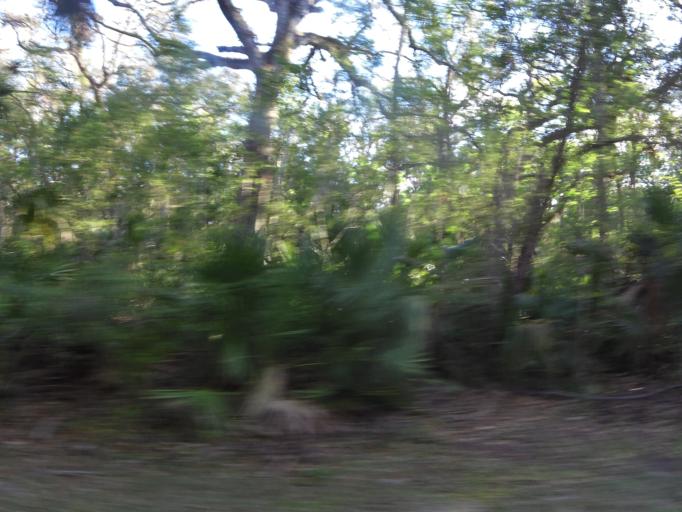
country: US
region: Florida
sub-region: Duval County
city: Atlantic Beach
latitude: 30.3722
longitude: -81.4029
